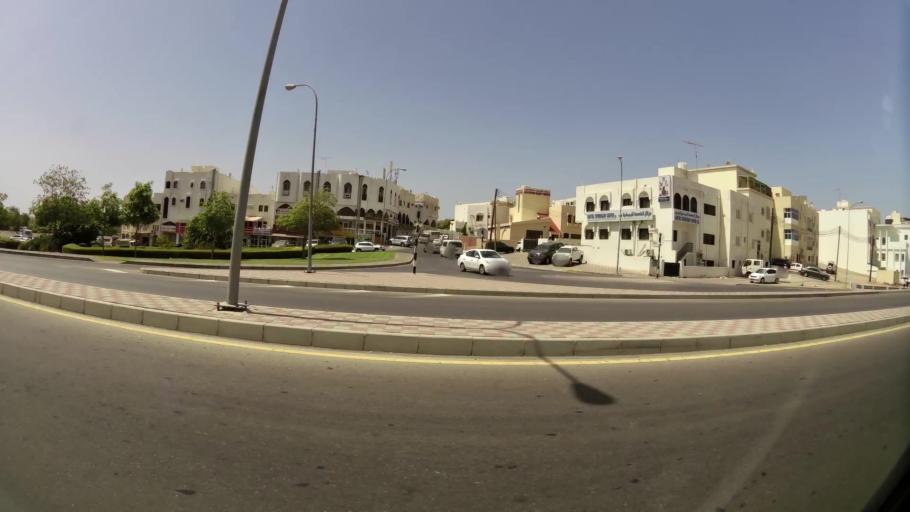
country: OM
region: Muhafazat Masqat
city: Muscat
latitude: 23.6181
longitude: 58.4963
